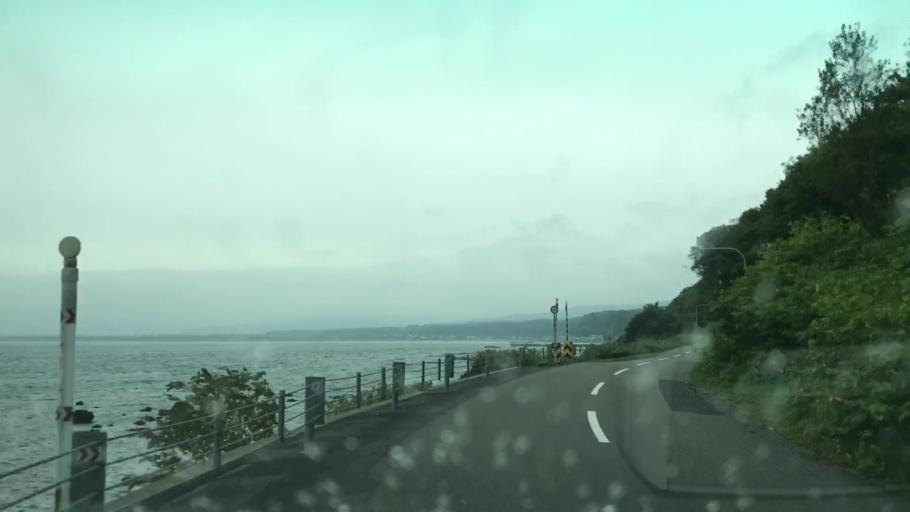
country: JP
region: Hokkaido
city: Iwanai
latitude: 42.7825
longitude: 140.2379
